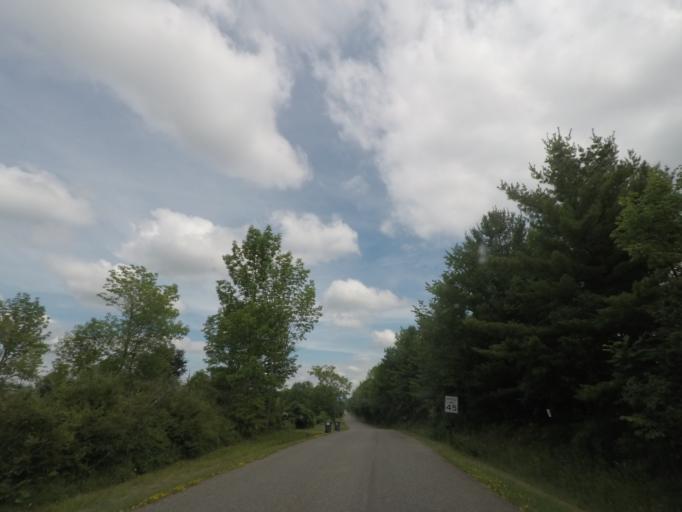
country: US
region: New York
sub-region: Saratoga County
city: Stillwater
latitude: 43.0122
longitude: -73.6427
